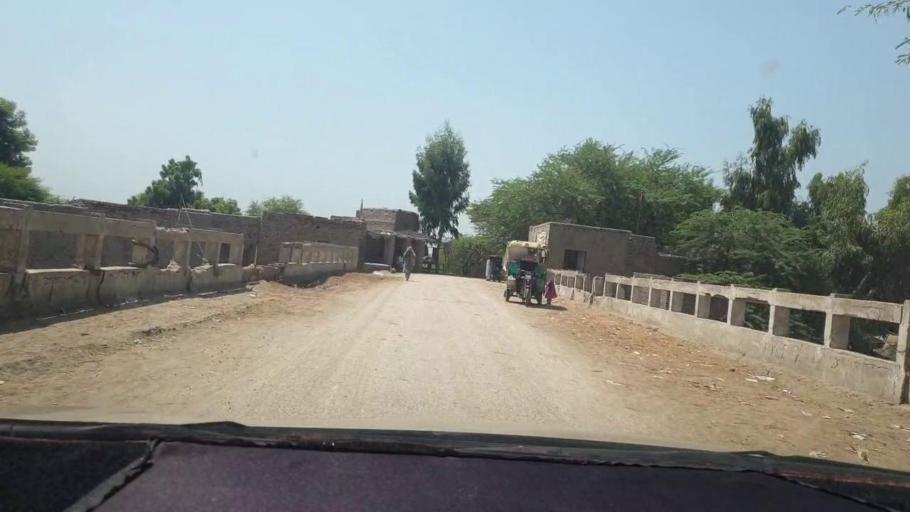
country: PK
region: Sindh
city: Kambar
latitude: 27.6122
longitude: 68.0497
